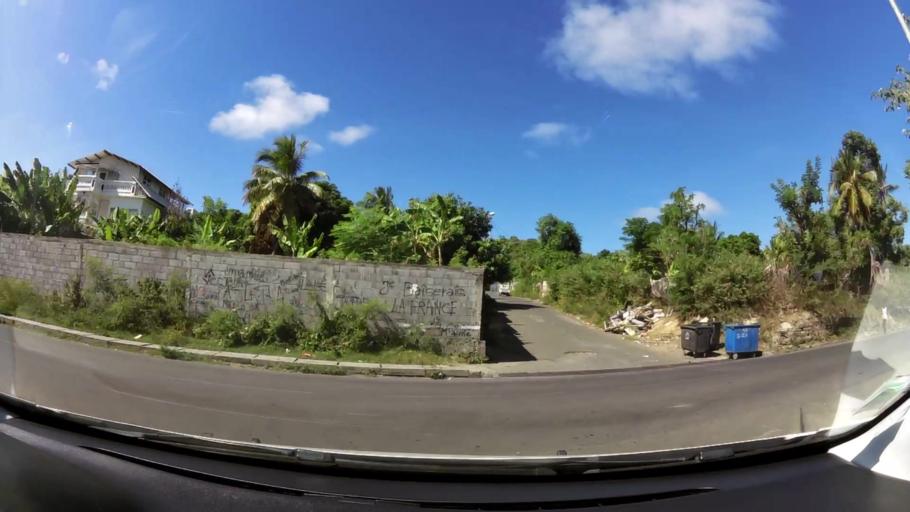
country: YT
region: Pamandzi
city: Pamandzi
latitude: -12.7892
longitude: 45.2799
